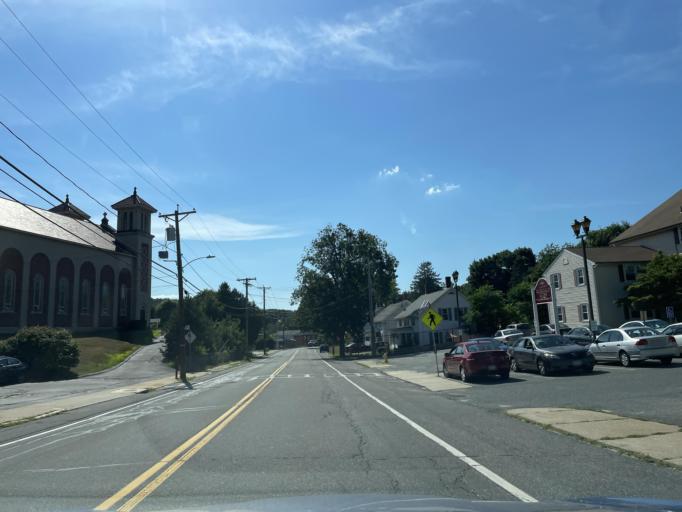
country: US
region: Massachusetts
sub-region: Worcester County
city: Northbridge
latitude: 42.1540
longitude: -71.6488
